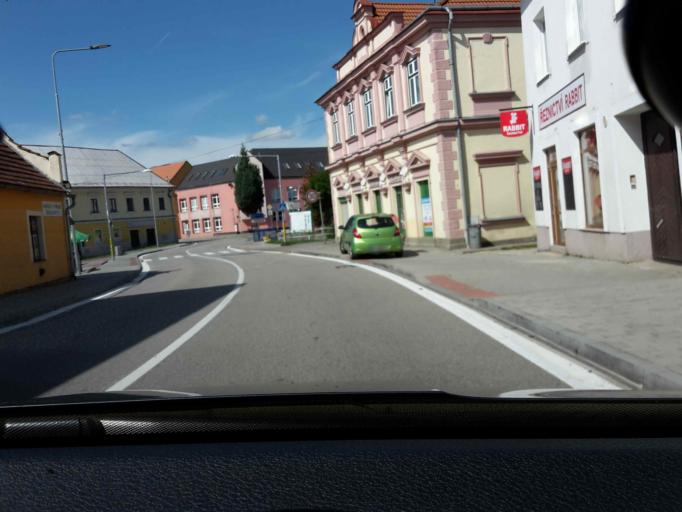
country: CZ
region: Jihocesky
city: Kardasova Recice
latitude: 49.1841
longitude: 14.8539
